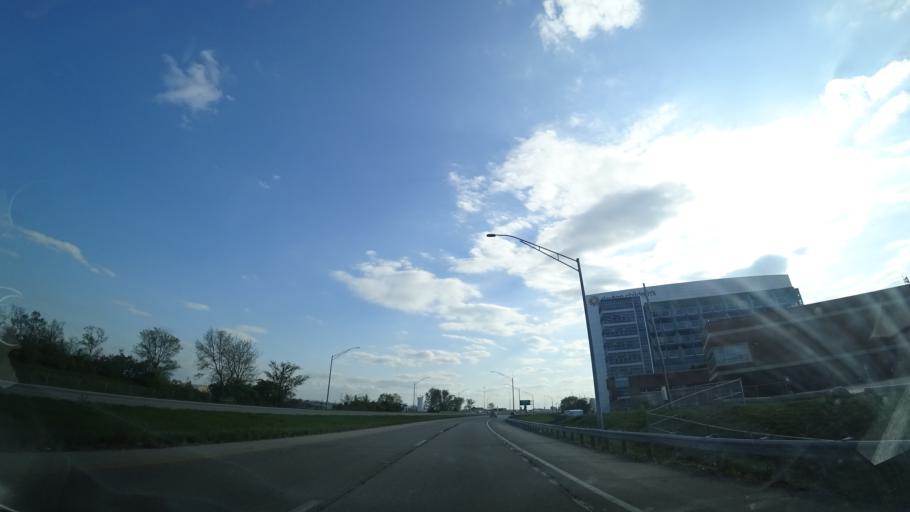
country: US
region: Ohio
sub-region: Montgomery County
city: Dayton
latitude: 39.7746
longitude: -84.1659
